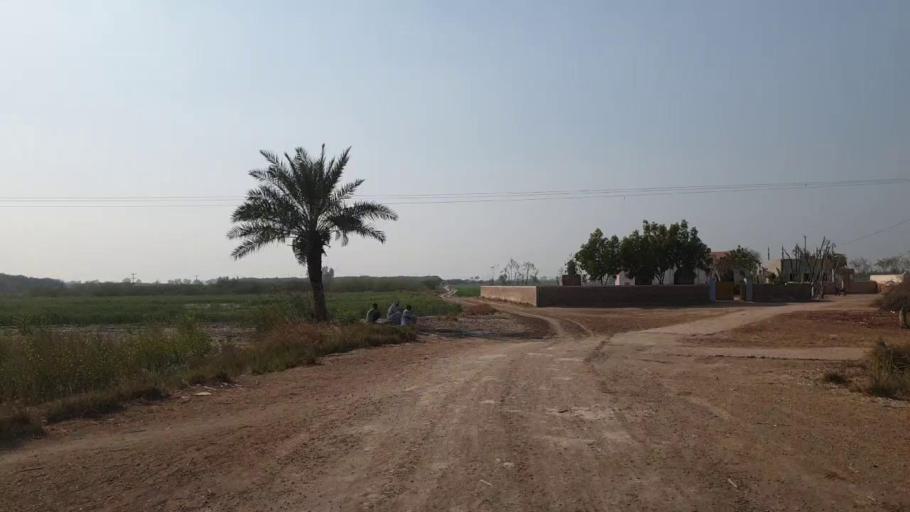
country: PK
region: Sindh
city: Tando Adam
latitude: 25.7157
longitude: 68.5651
